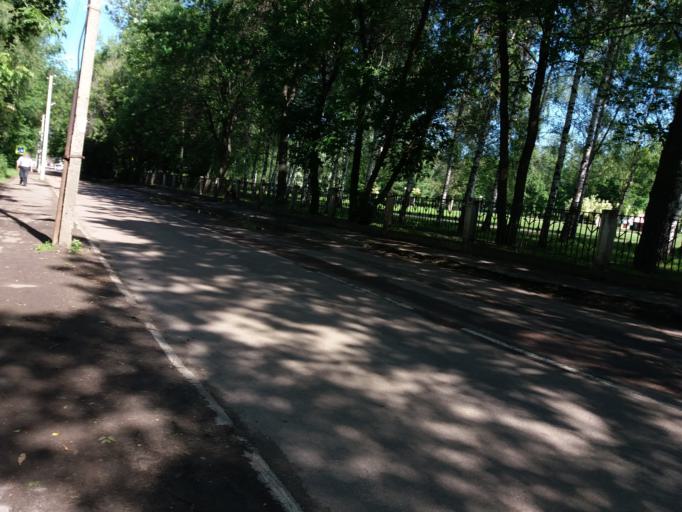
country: RU
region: Jaroslavl
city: Yaroslavl
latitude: 57.6361
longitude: 39.8526
